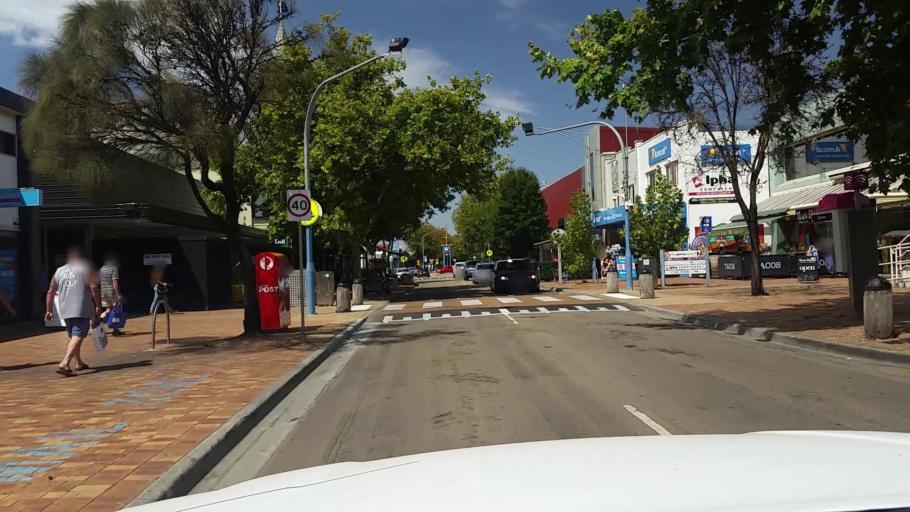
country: AU
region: Victoria
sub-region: Mornington Peninsula
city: Mornington
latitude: -38.2196
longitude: 145.0387
